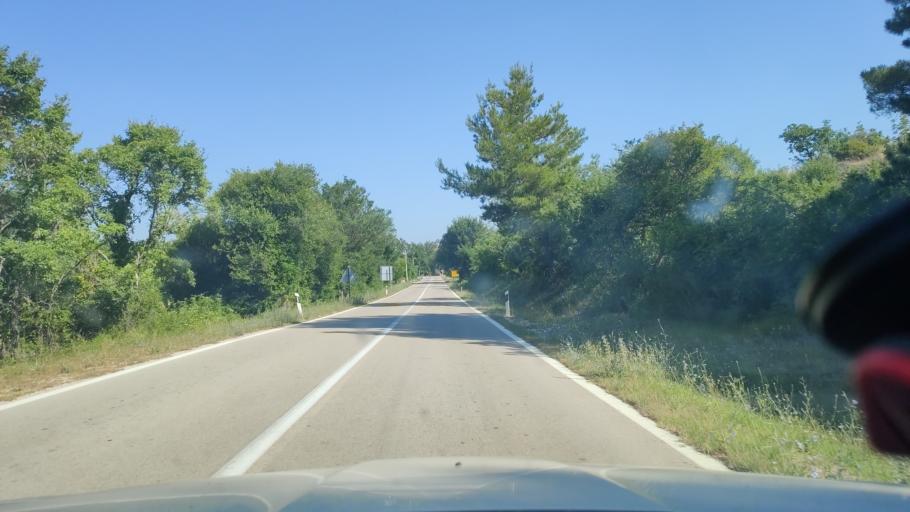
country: HR
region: Sibensko-Kniniska
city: Zaton
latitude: 43.9265
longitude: 15.8148
